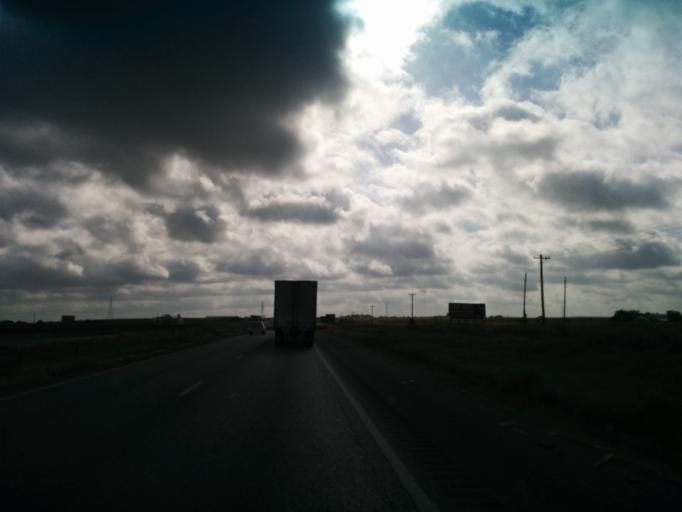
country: US
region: Texas
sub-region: Guadalupe County
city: Marion
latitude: 29.5325
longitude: -98.0987
